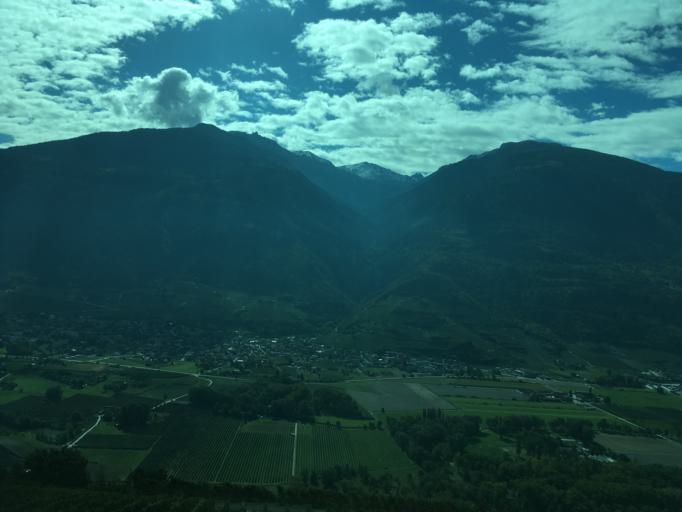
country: CH
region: Valais
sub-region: Sierre District
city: Chermignon-d'en Haut
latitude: 46.2770
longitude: 7.4832
